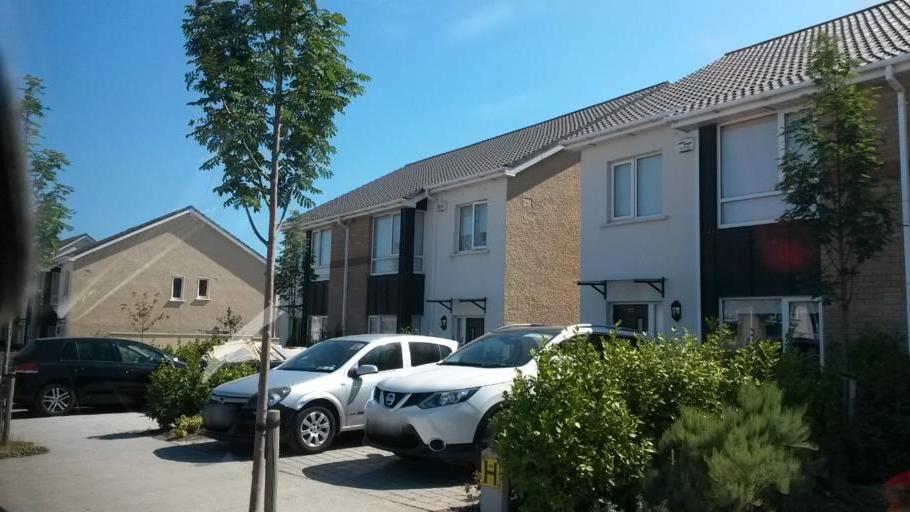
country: IE
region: Leinster
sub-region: Fingal County
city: Swords
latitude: 53.4481
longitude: -6.2522
